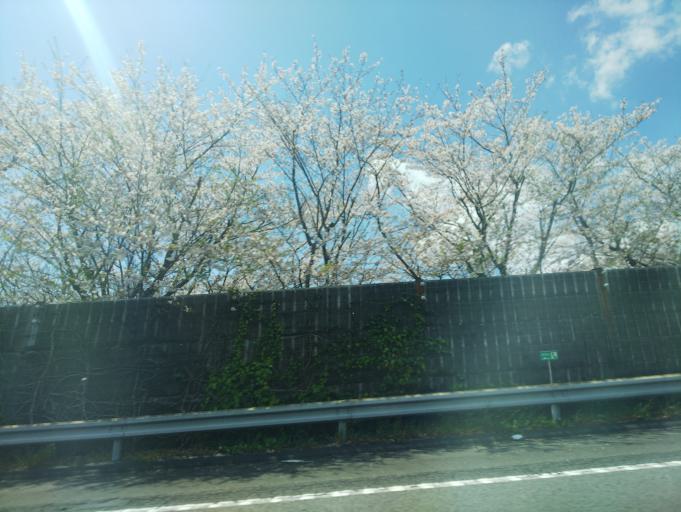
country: JP
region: Shizuoka
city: Shizuoka-shi
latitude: 34.9776
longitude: 138.4314
